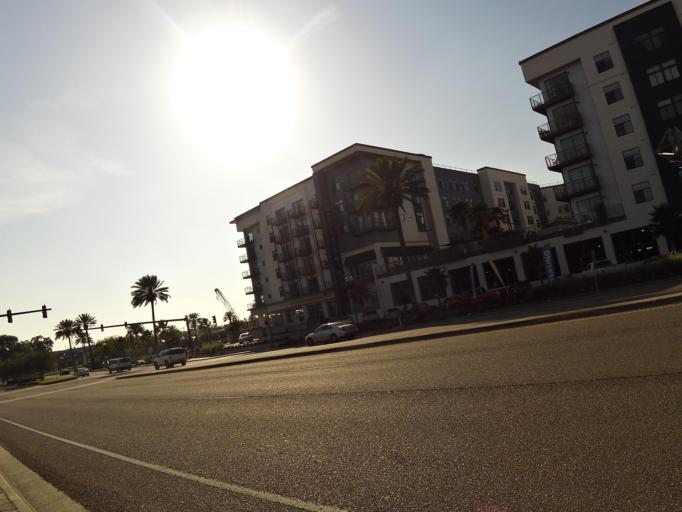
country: US
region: Florida
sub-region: Duval County
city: Jacksonville
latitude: 30.3219
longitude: -81.6727
